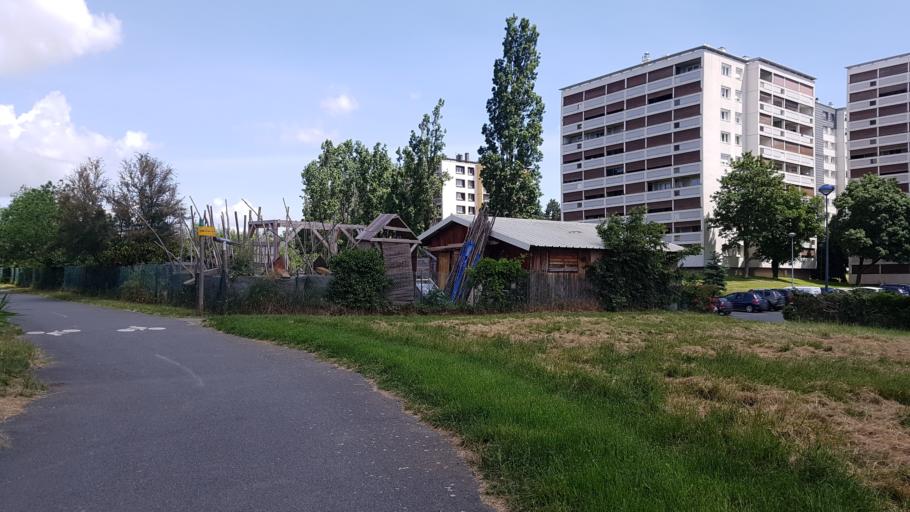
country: FR
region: Rhone-Alpes
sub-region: Departement du Rhone
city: Rillieux-la-Pape
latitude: 45.8212
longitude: 4.9045
